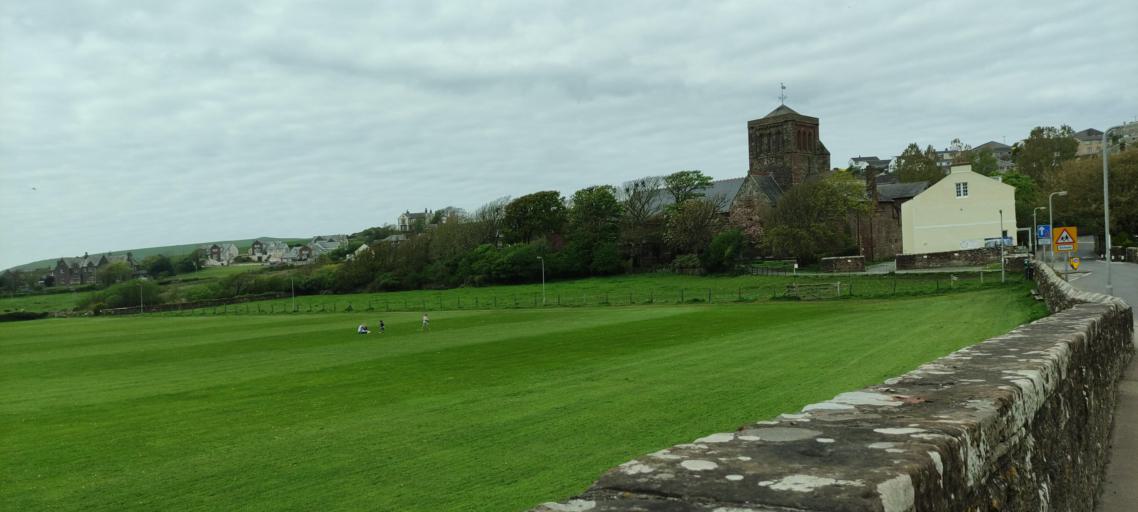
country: GB
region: England
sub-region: Cumbria
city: Saint Bees
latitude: 54.4931
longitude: -3.5915
